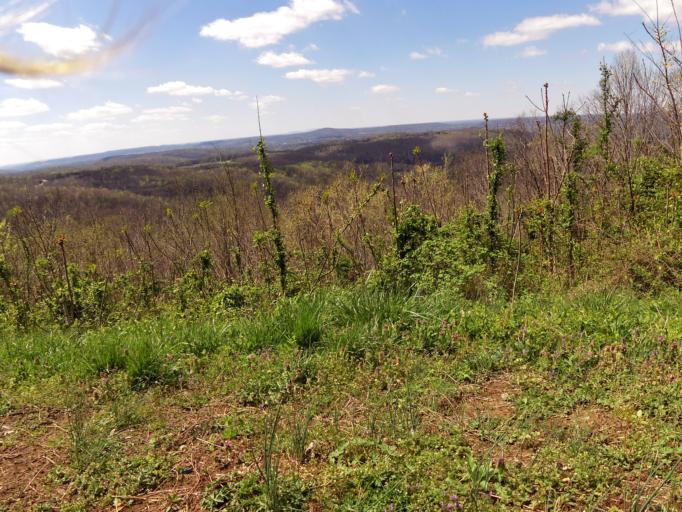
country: US
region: Tennessee
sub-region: White County
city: Sparta
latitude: 35.9290
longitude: -85.3825
